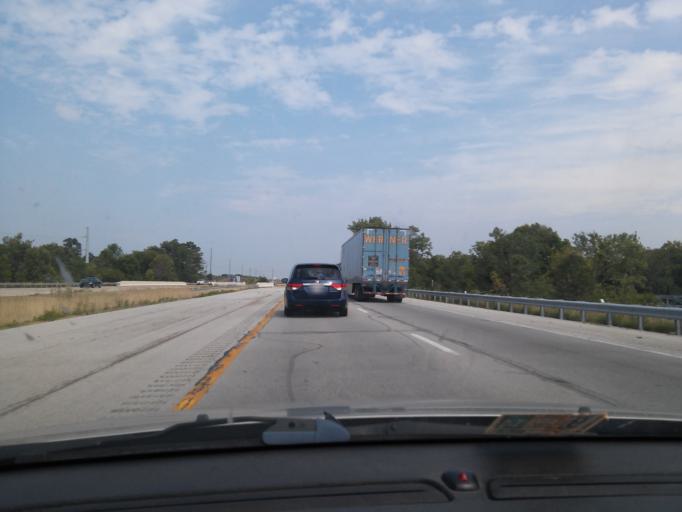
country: US
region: Ohio
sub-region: Preble County
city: Lewisburg
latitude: 39.8360
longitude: -84.5827
